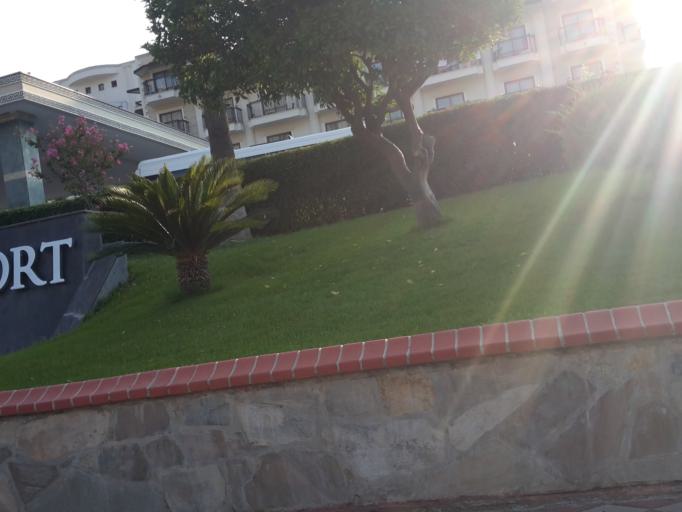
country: TR
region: Antalya
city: Kemer
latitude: 36.6140
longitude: 30.5565
